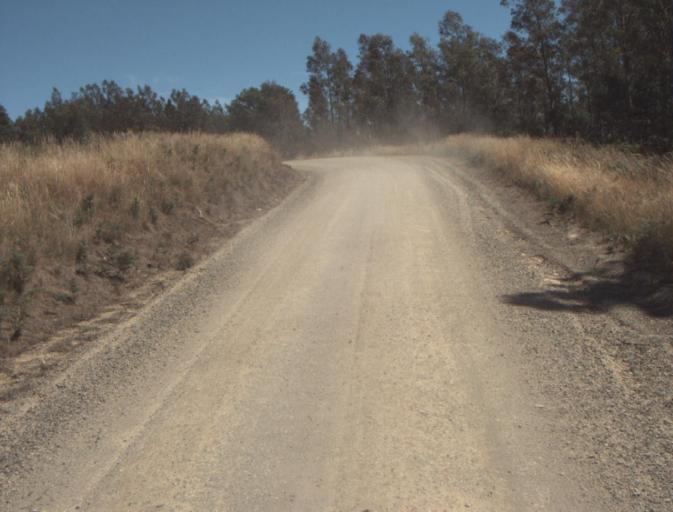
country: AU
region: Tasmania
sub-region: Dorset
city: Scottsdale
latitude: -41.3301
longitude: 147.4378
